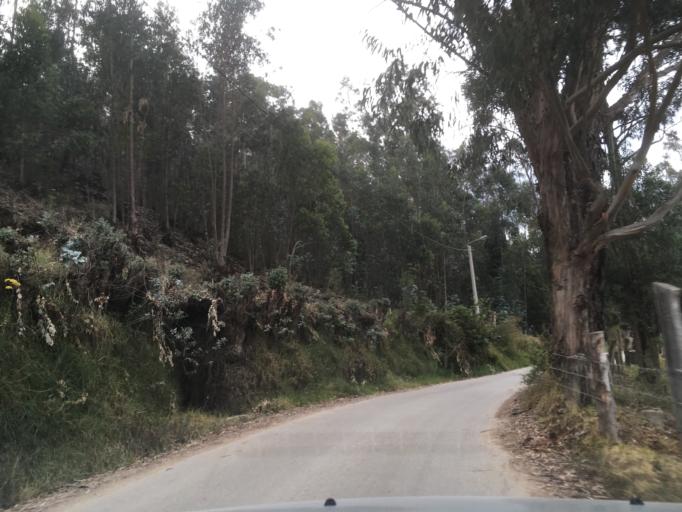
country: CO
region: Boyaca
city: Firavitoba
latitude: 5.6727
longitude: -73.0021
